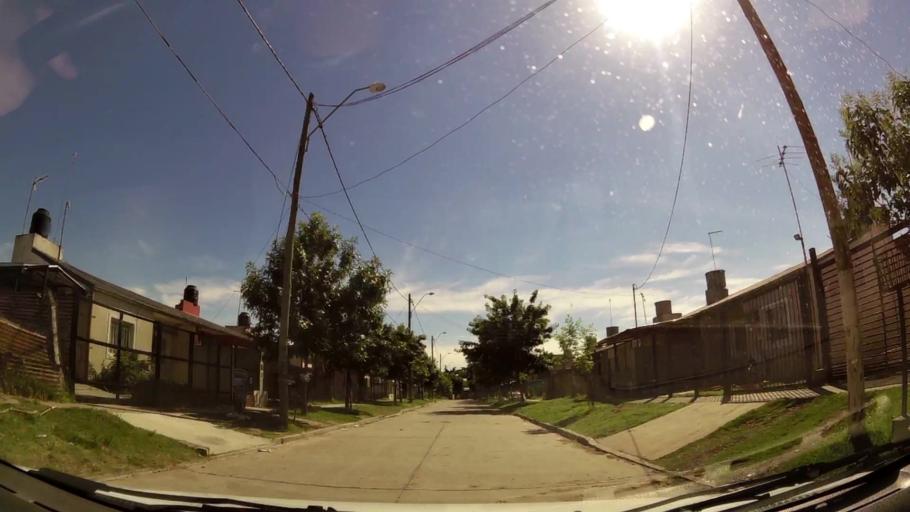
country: AR
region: Buenos Aires
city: Hurlingham
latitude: -34.6191
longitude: -58.6530
